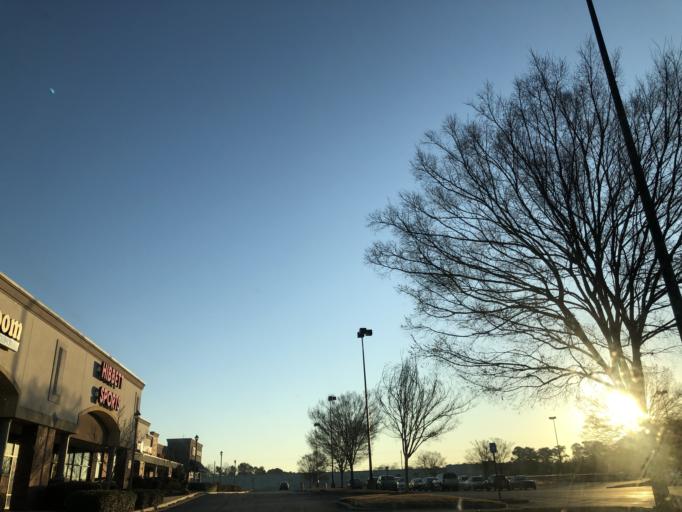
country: US
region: Georgia
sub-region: Clayton County
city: Conley
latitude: 33.6354
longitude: -84.2899
